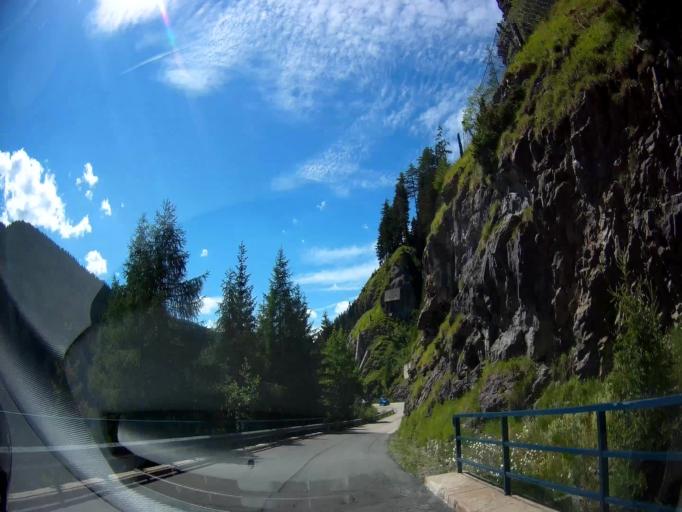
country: AT
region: Carinthia
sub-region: Politischer Bezirk Sankt Veit an der Glan
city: Glodnitz
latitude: 46.9366
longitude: 14.0499
